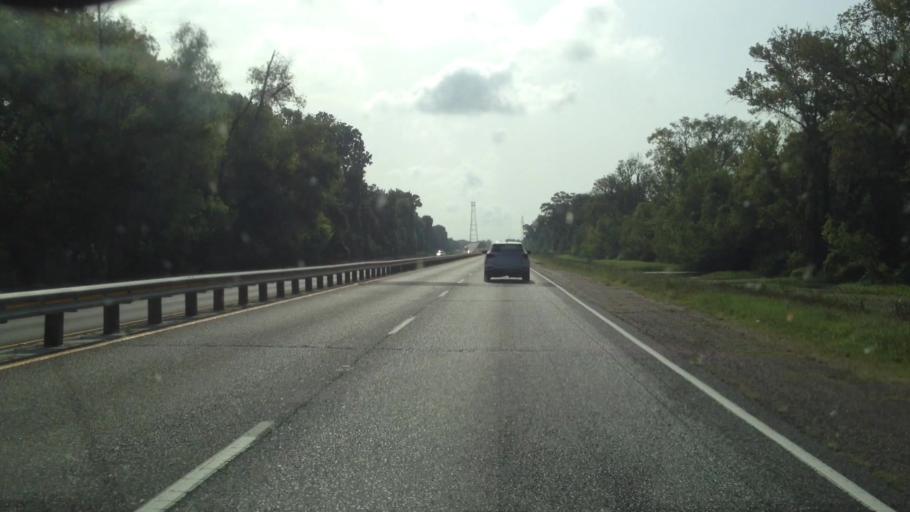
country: US
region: Louisiana
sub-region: Pointe Coupee Parish
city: Livonia
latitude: 30.5554
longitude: -91.5899
